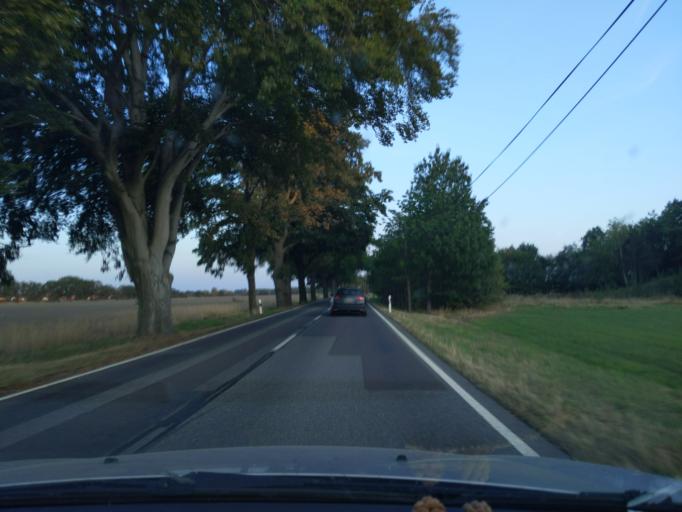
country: DE
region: Saxony
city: Hoyerswerda
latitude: 51.4681
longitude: 14.2043
